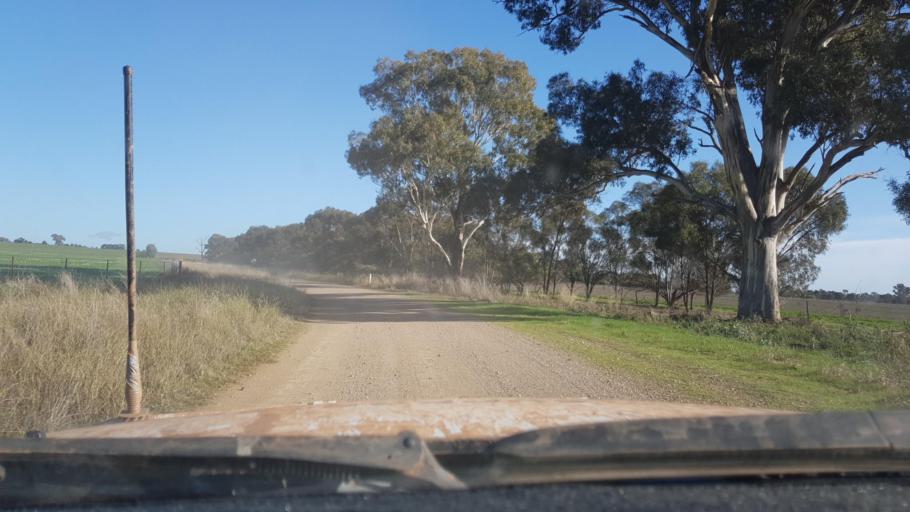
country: AU
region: New South Wales
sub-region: Junee
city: Junee
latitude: -34.9682
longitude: 147.8062
